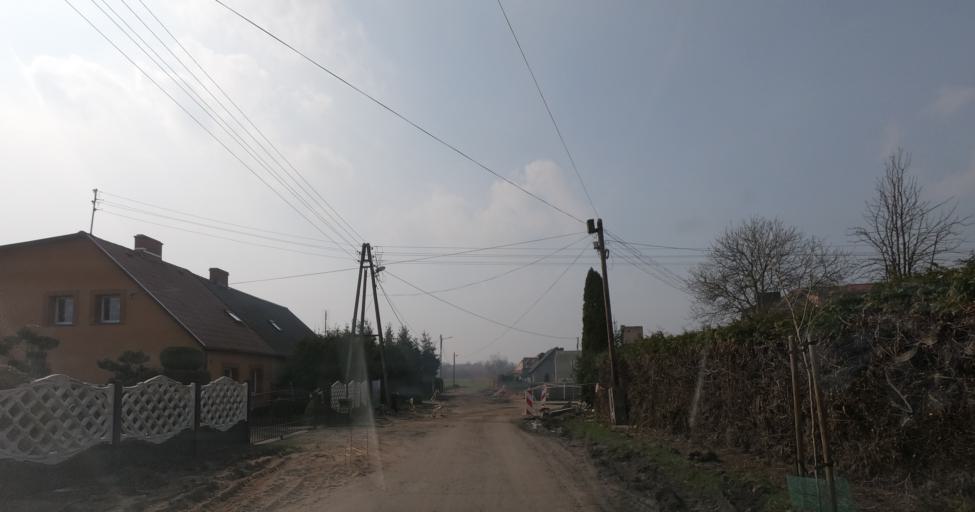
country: PL
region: West Pomeranian Voivodeship
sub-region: Powiat gryfinski
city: Chojna
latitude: 52.9514
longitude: 14.4365
